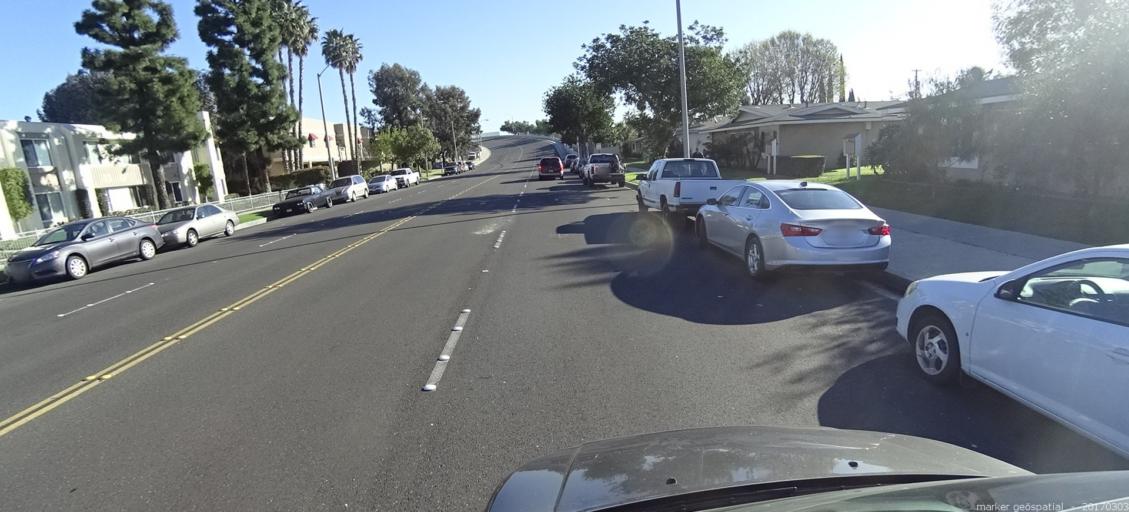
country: US
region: California
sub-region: Orange County
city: Placentia
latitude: 33.8517
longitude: -117.8875
